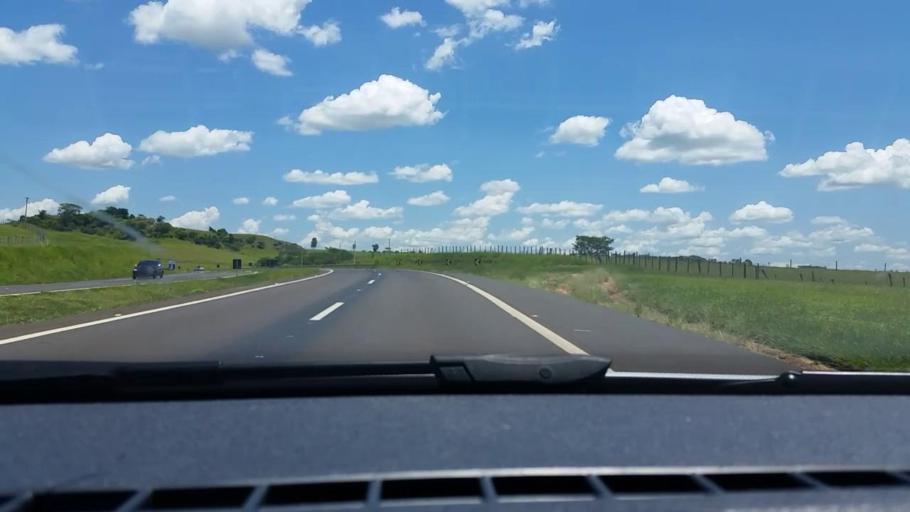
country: BR
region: Sao Paulo
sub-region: Bauru
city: Bauru
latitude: -22.4271
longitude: -49.1301
